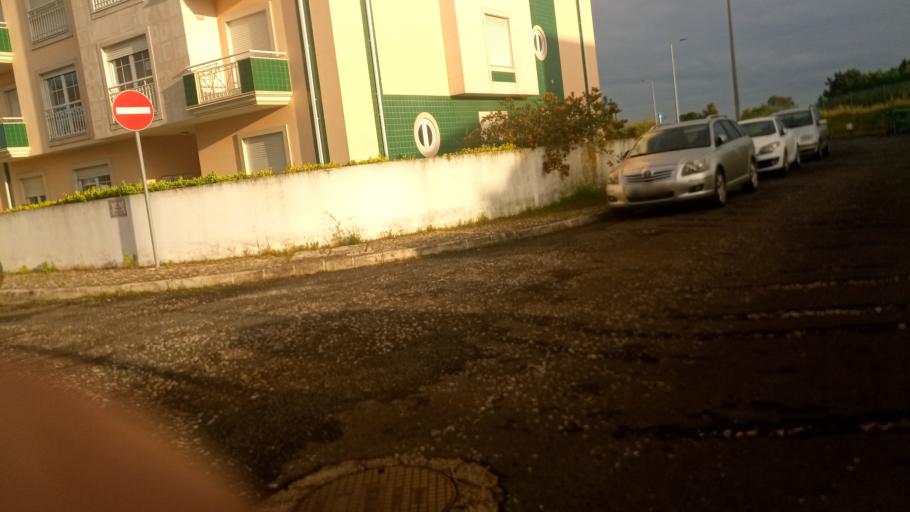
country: PT
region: Leiria
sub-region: Caldas da Rainha
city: Caldas da Rainha
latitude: 39.4144
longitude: -9.1380
